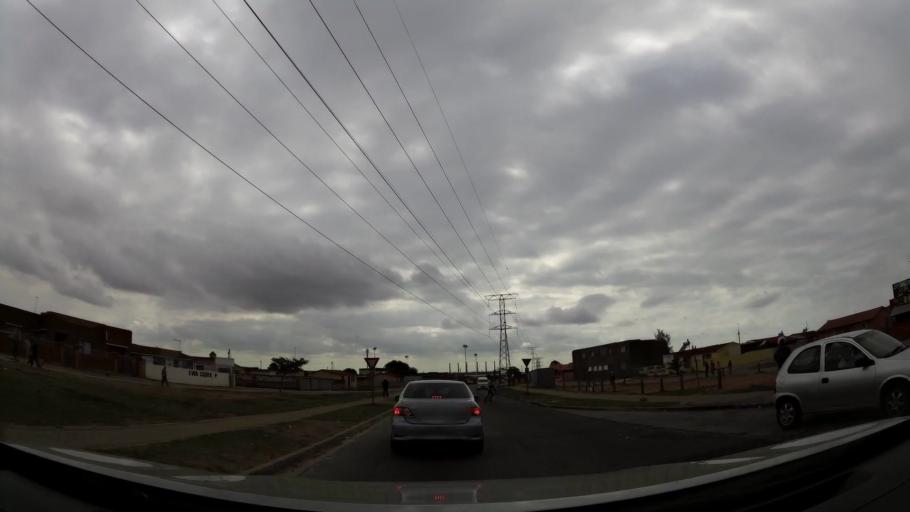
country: ZA
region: Eastern Cape
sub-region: Nelson Mandela Bay Metropolitan Municipality
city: Port Elizabeth
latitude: -33.8885
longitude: 25.5950
